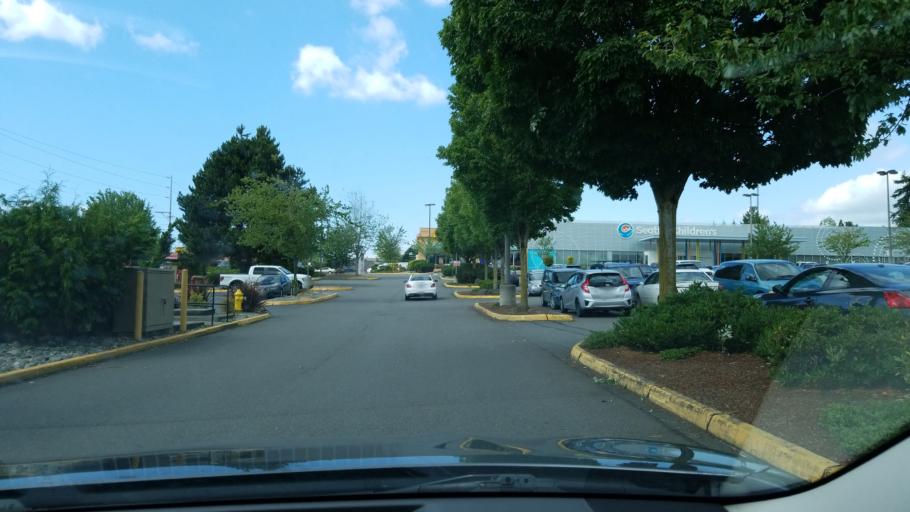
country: US
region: Washington
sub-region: King County
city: Lakeland South
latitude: 47.2878
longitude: -122.3126
